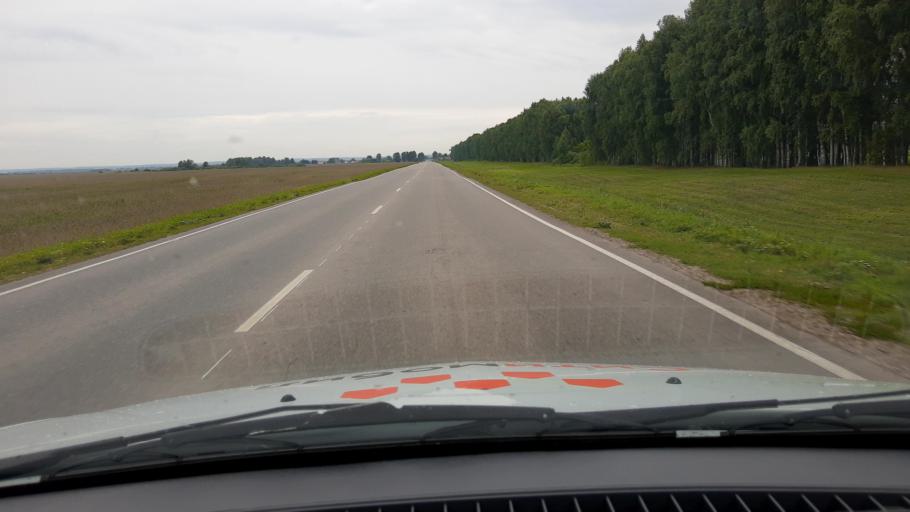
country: RU
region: Bashkortostan
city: Krasnaya Gorka
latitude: 55.1045
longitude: 56.6281
